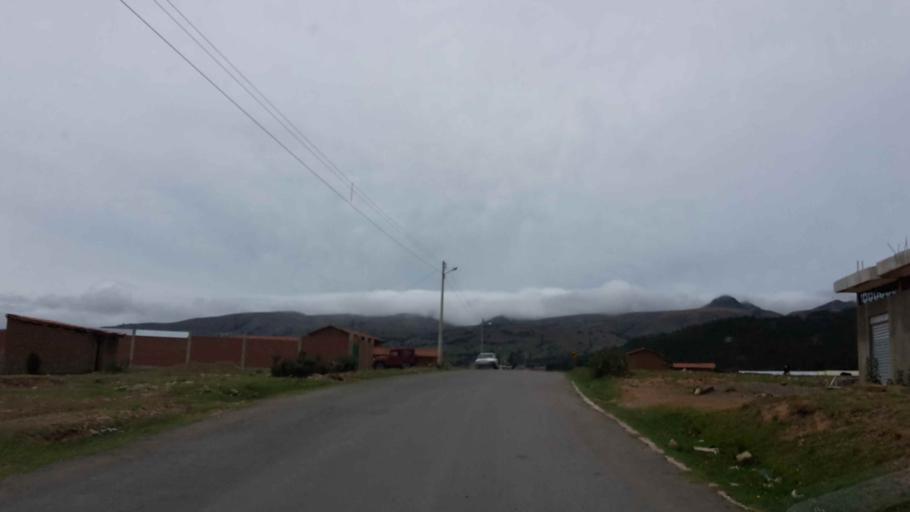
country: BO
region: Cochabamba
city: Arani
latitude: -17.4549
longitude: -65.7189
